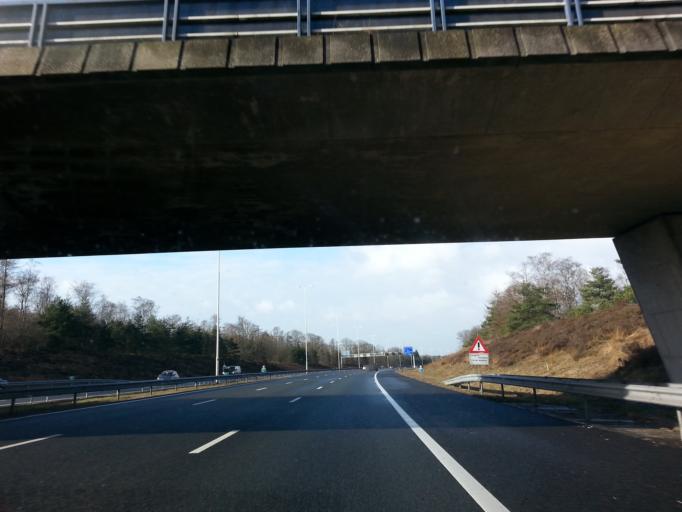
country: NL
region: Utrecht
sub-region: Gemeente Soest
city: Soest
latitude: 52.1182
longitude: 5.3268
